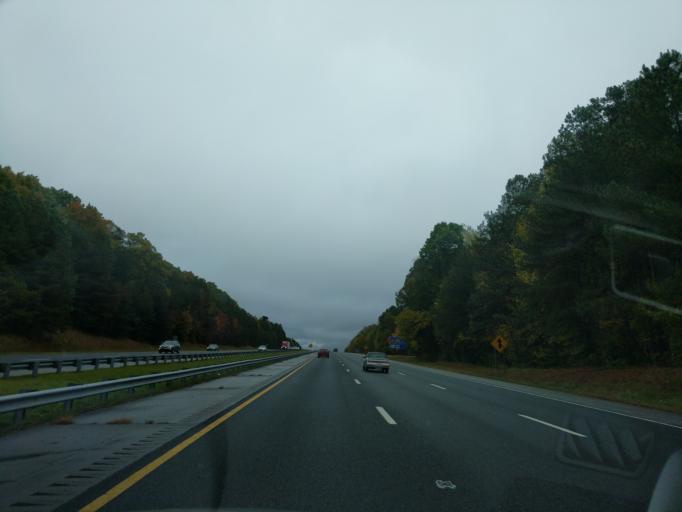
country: US
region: North Carolina
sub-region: Orange County
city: Hillsborough
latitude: 36.0591
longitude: -79.1250
